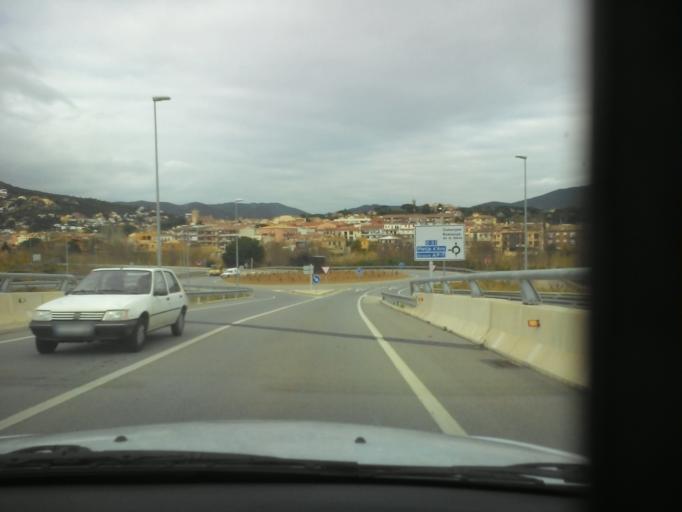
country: ES
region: Catalonia
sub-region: Provincia de Girona
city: Calonge
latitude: 41.8566
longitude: 3.0786
